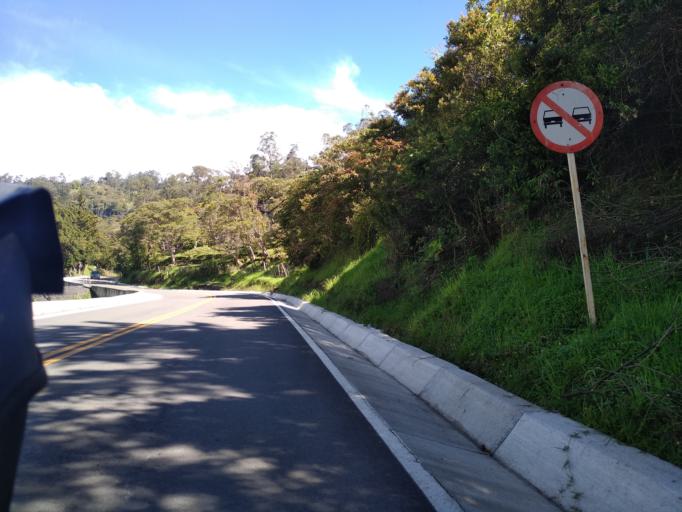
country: CO
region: Santander
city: Velez
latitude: 6.0001
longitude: -73.6914
